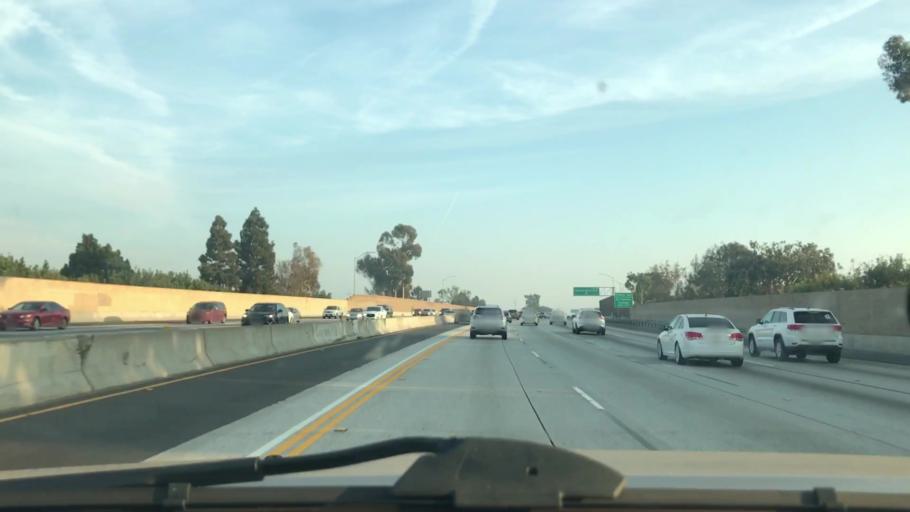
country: US
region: California
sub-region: Los Angeles County
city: Lawndale
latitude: 33.8814
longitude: -118.3486
